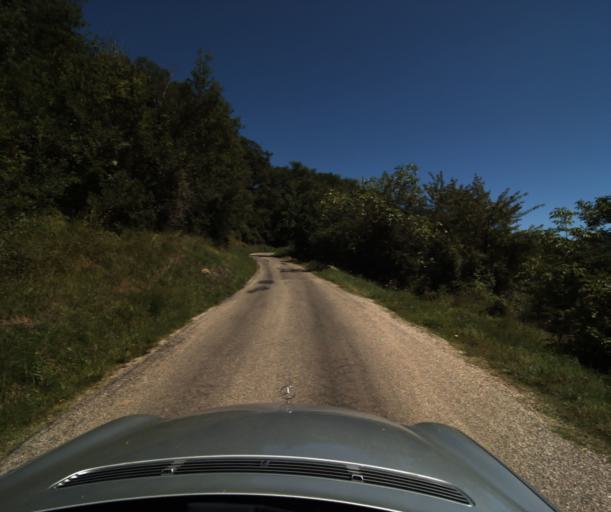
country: FR
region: Midi-Pyrenees
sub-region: Departement de l'Ariege
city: Belesta
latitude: 42.9614
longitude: 1.9264
